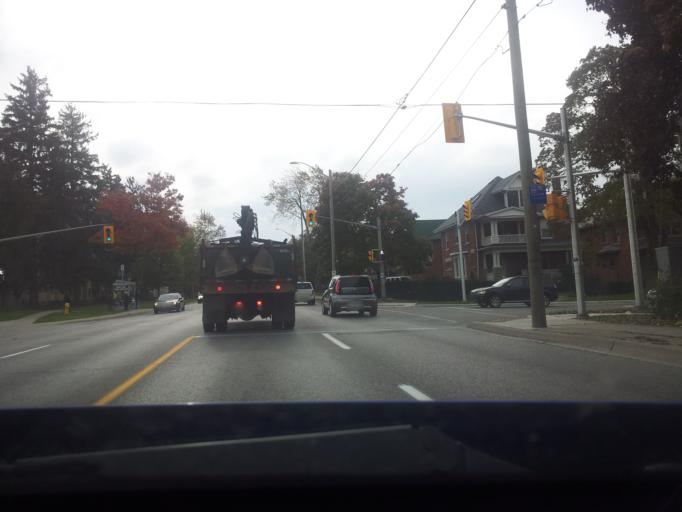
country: CA
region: Ontario
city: London
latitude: 43.0020
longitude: -81.2566
